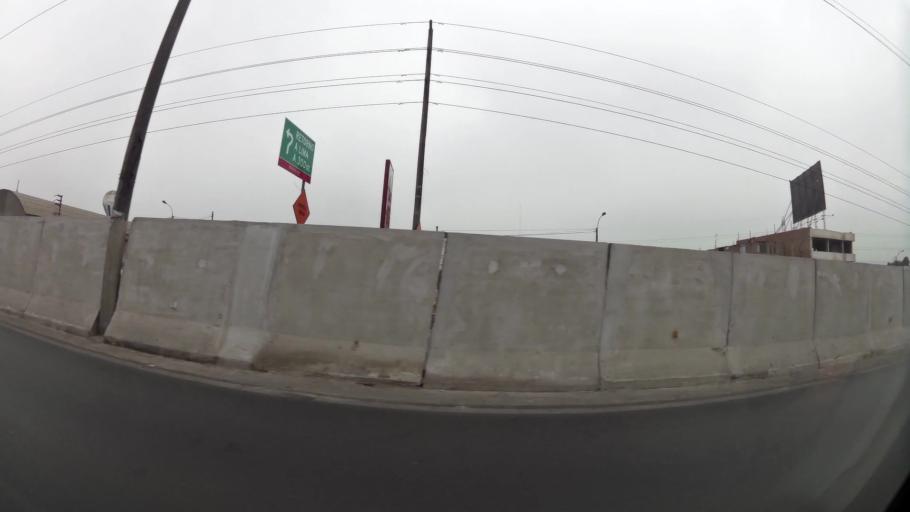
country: PE
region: Lima
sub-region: Lima
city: Urb. Santo Domingo
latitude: -11.8991
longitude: -77.0679
